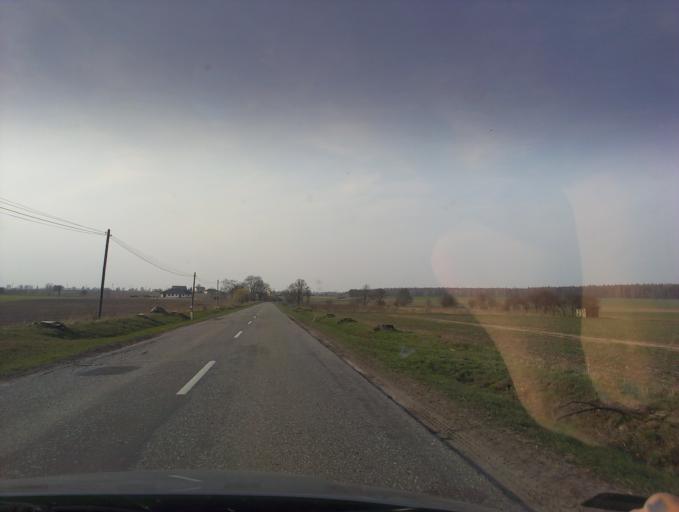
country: PL
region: Greater Poland Voivodeship
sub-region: Powiat zlotowski
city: Lipka
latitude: 53.5011
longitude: 17.2475
